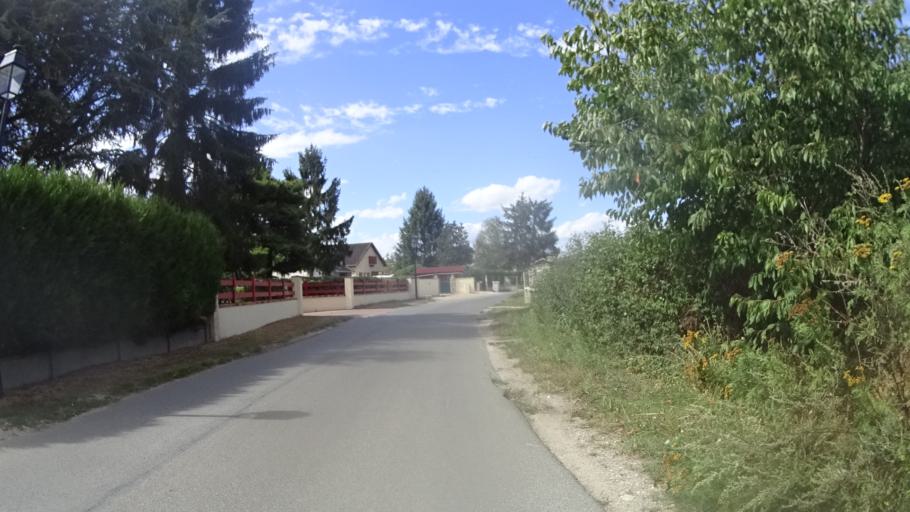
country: FR
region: Ile-de-France
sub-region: Departement de l'Essonne
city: Boutigny-sur-Essonne
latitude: 48.4154
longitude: 2.3930
